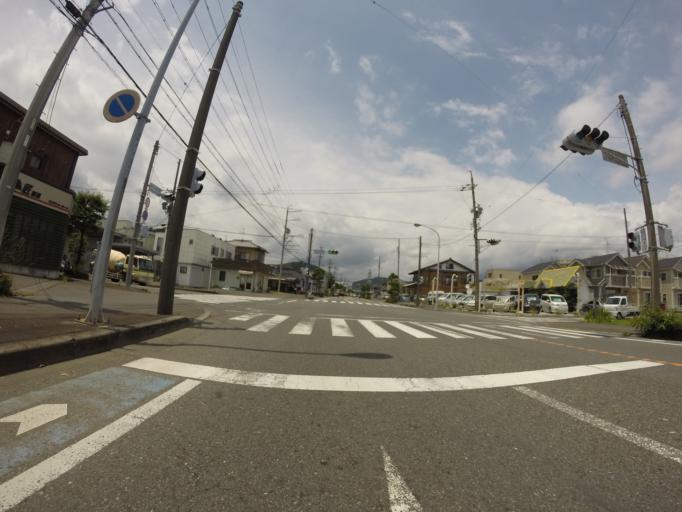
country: JP
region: Shizuoka
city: Shizuoka-shi
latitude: 34.9699
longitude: 138.3507
